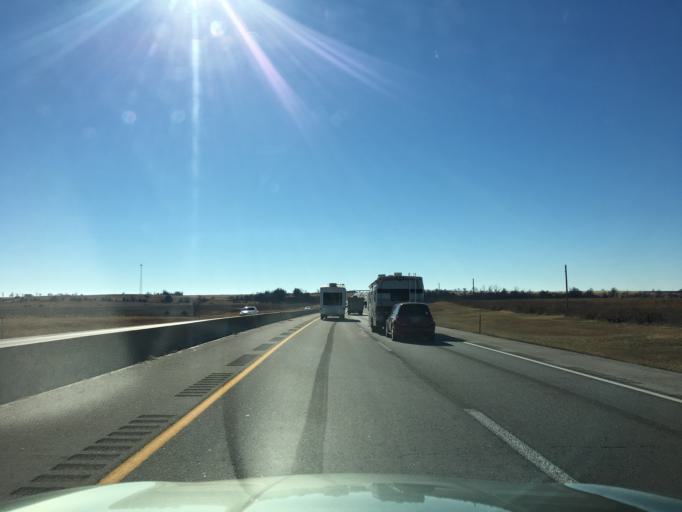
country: US
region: Oklahoma
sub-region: Kay County
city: Blackwell
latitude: 37.0124
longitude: -97.3387
